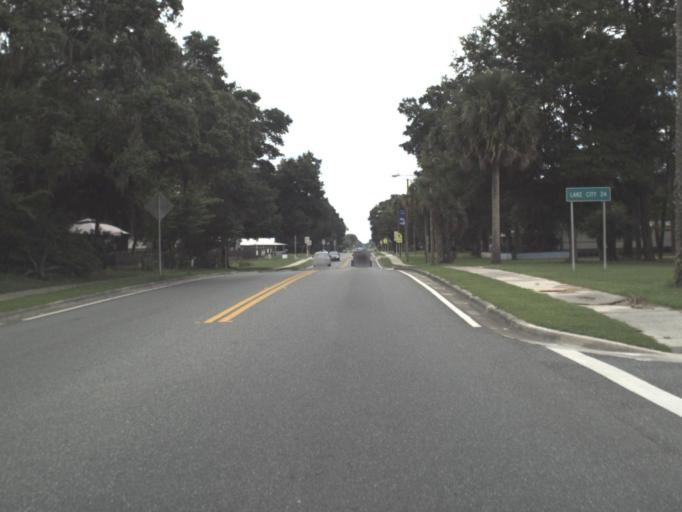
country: US
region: Florida
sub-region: Lafayette County
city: Mayo
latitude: 29.9598
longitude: -82.9269
